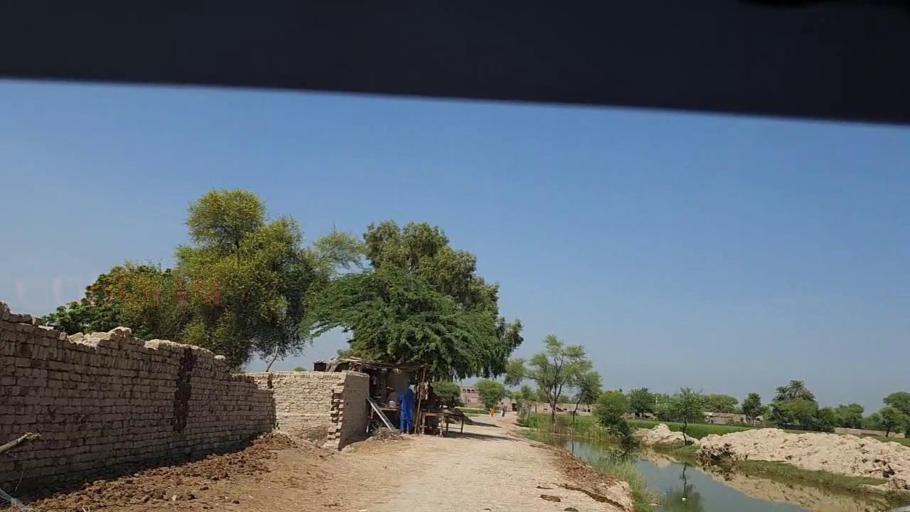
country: PK
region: Sindh
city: Tangwani
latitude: 28.2835
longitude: 69.0376
